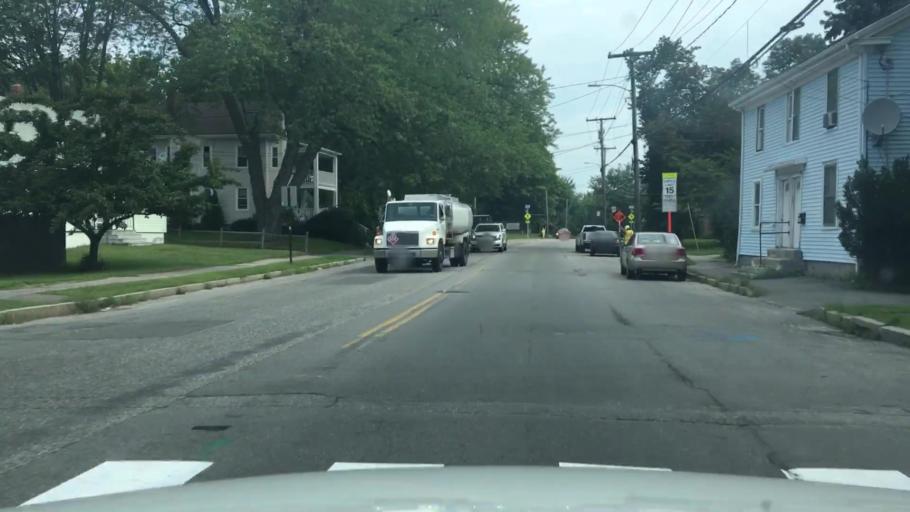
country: US
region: Maine
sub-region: Cumberland County
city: Portland
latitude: 43.6938
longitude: -70.2923
